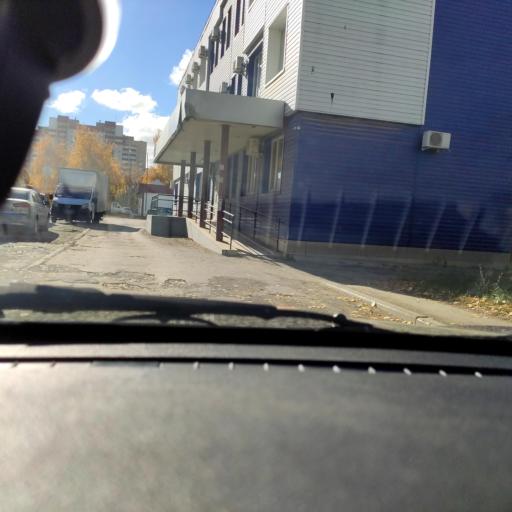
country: RU
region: Samara
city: Tol'yatti
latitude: 53.5269
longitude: 49.3175
